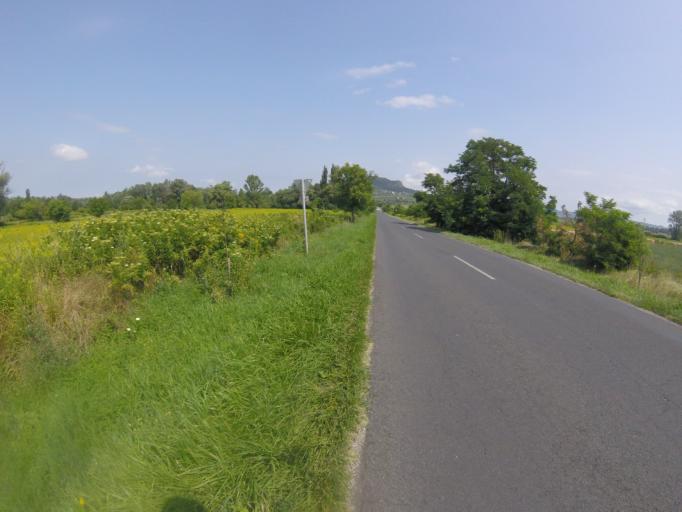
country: HU
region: Veszprem
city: Badacsonytomaj
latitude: 46.8126
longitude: 17.4476
